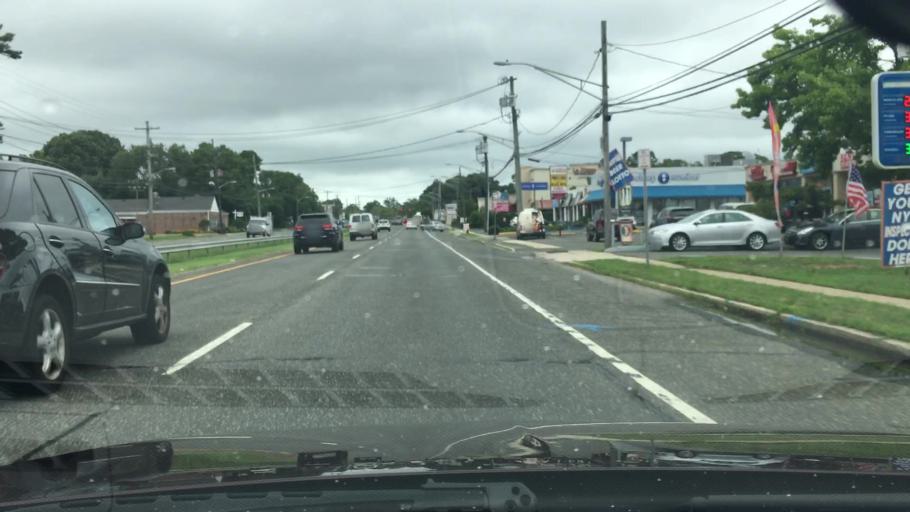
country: US
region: New York
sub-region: Suffolk County
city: South Huntington
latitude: 40.8107
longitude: -73.4094
